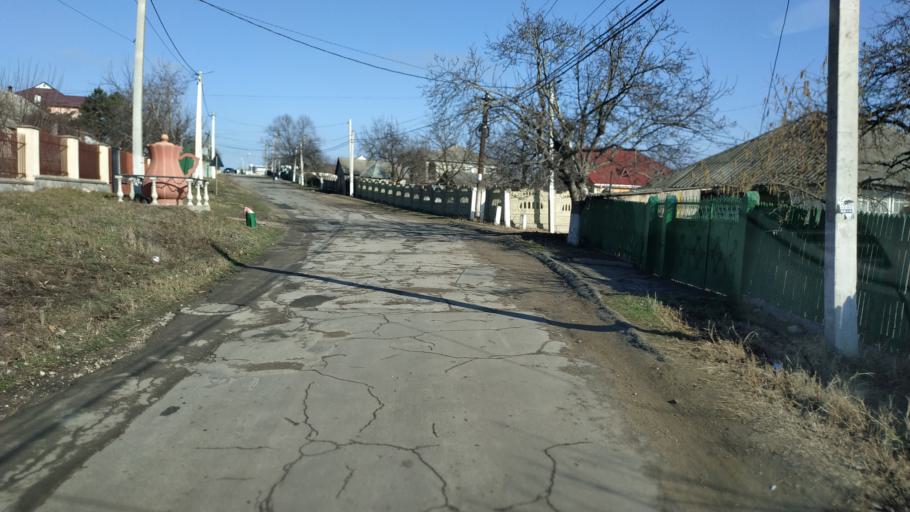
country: MD
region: Laloveni
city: Ialoveni
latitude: 46.9425
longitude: 28.7236
